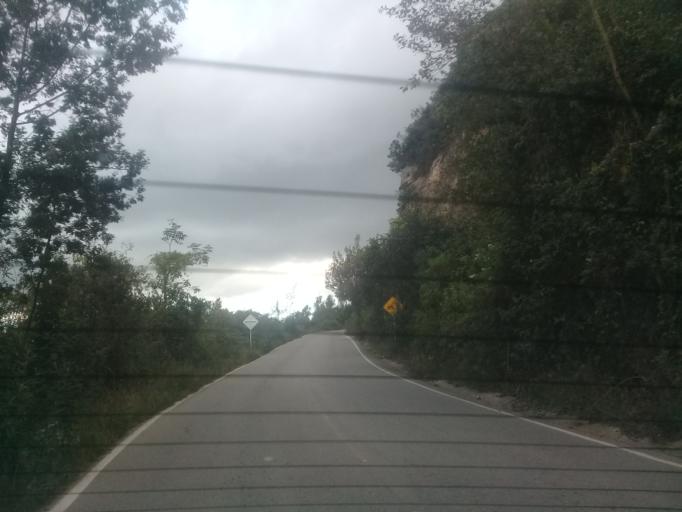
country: CO
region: Cundinamarca
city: Tabio
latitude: 4.9405
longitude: -74.1098
